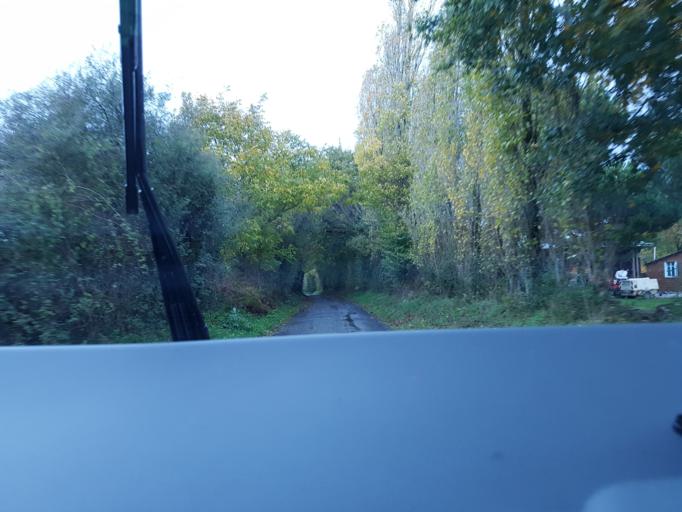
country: FR
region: Poitou-Charentes
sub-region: Departement des Deux-Sevres
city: Lezay
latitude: 46.2230
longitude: -0.0367
